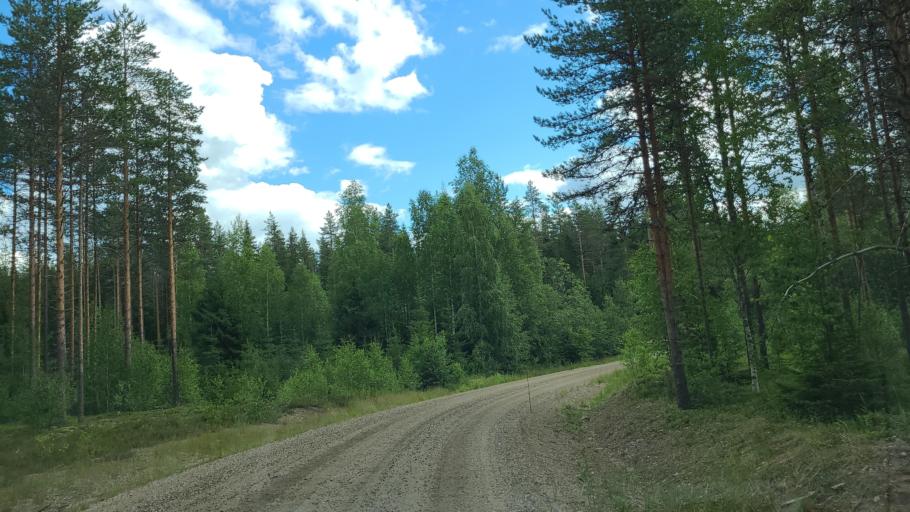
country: FI
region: Northern Savo
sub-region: Koillis-Savo
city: Kaavi
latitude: 63.0357
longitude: 28.7898
